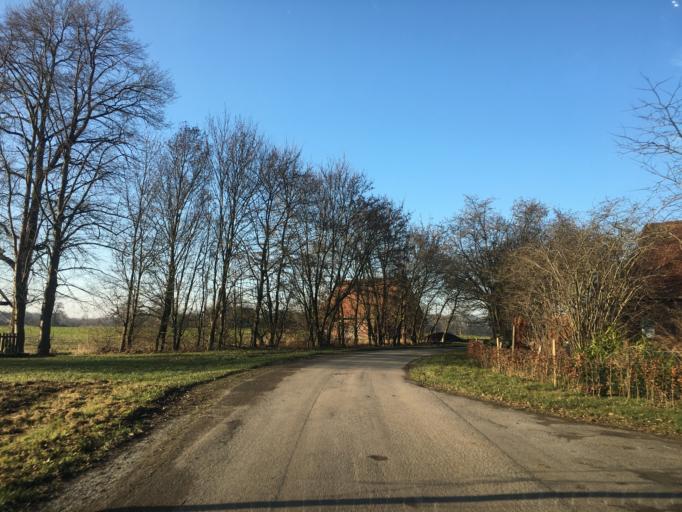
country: DE
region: North Rhine-Westphalia
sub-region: Regierungsbezirk Munster
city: Altenberge
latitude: 52.0349
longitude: 7.5308
